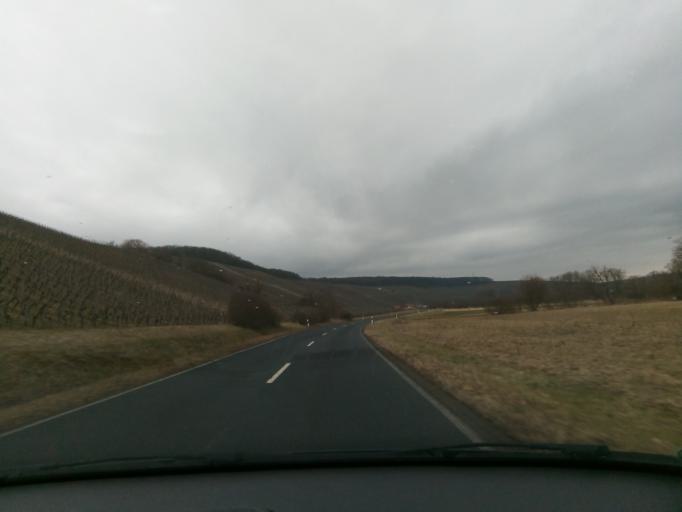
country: DE
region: Bavaria
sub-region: Regierungsbezirk Unterfranken
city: Nordheim
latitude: 49.8377
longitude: 10.1750
